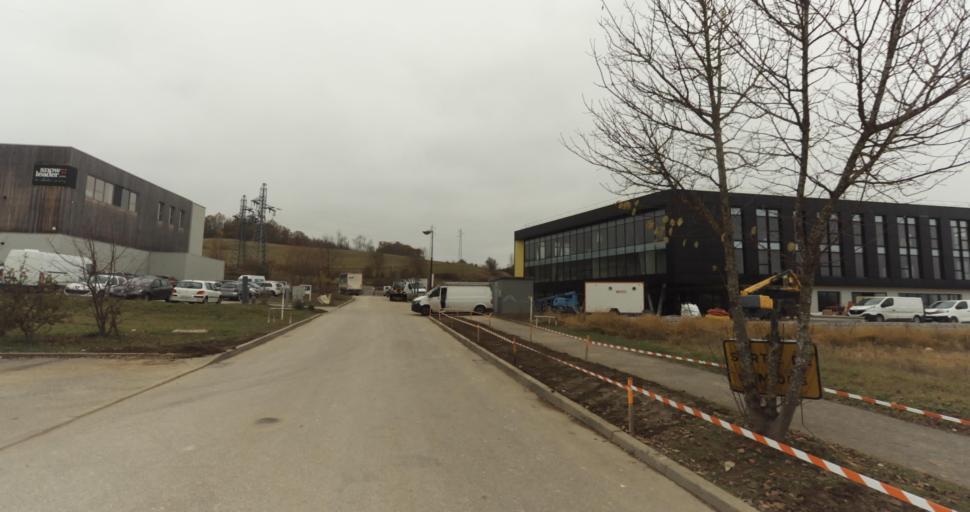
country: FR
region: Rhone-Alpes
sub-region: Departement de la Haute-Savoie
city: Seynod
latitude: 45.8926
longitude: 6.0756
